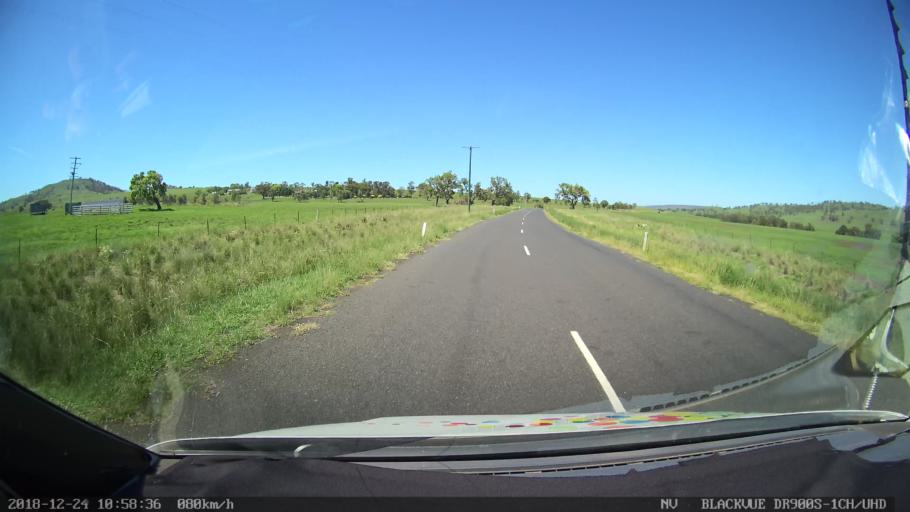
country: AU
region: New South Wales
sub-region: Upper Hunter Shire
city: Merriwa
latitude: -32.0495
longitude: 150.4056
